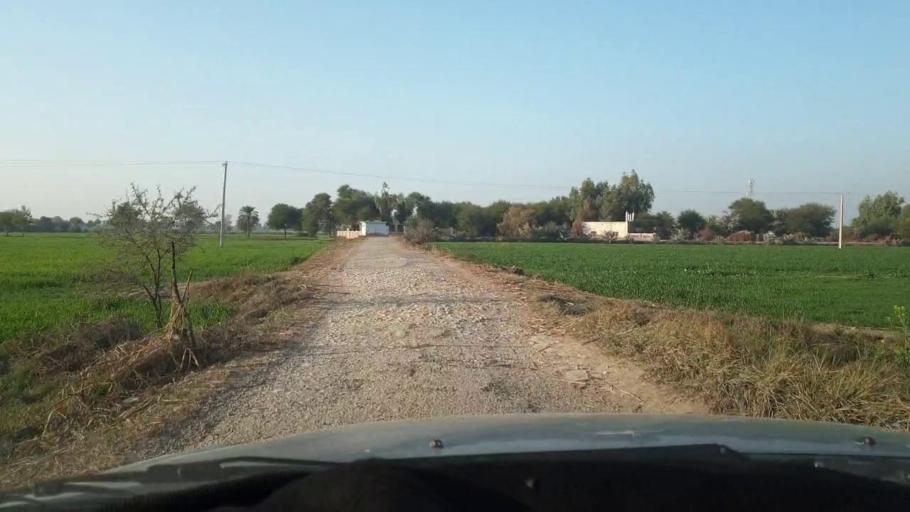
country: PK
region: Sindh
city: Mirpur Mathelo
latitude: 27.9825
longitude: 69.6282
